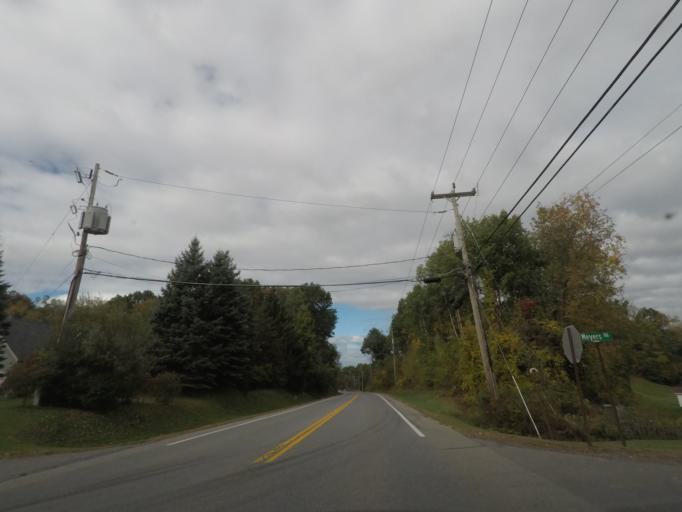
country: US
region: New York
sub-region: Saratoga County
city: Country Knolls
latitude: 42.8871
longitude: -73.7686
